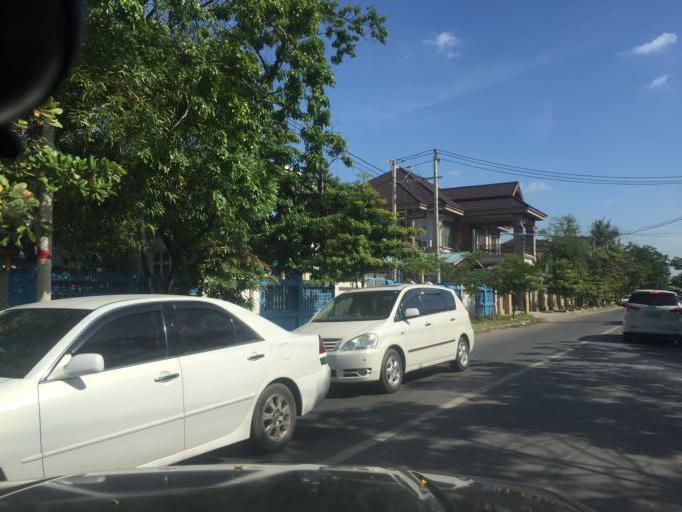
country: MM
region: Mandalay
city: Mandalay
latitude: 21.9516
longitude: 96.1082
